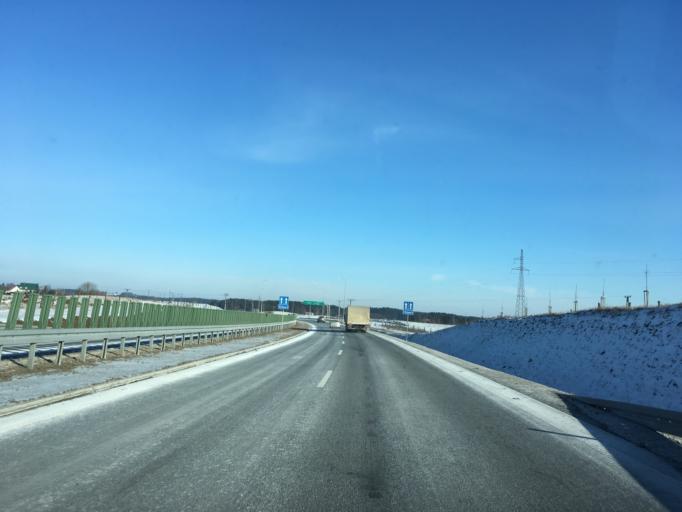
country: PL
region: Pomeranian Voivodeship
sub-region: Powiat koscierski
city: Koscierzyna
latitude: 54.1073
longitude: 17.9666
